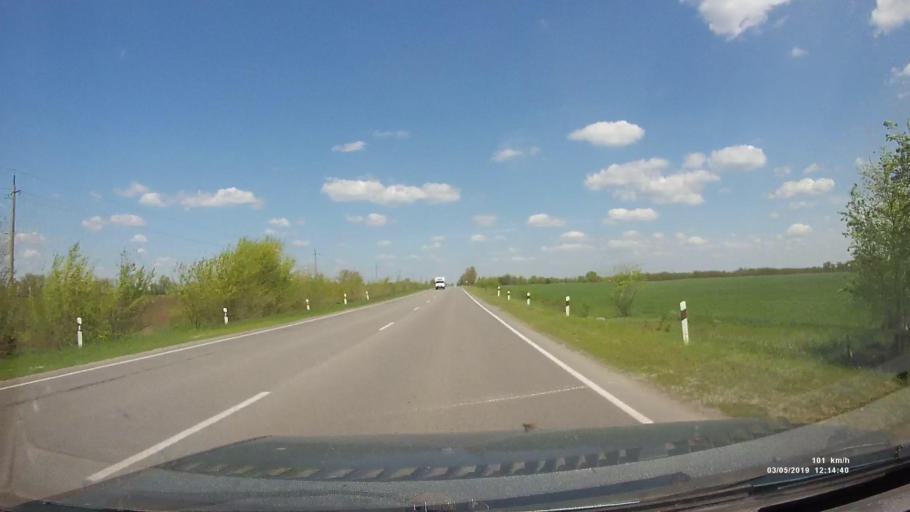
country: RU
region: Rostov
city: Melikhovskaya
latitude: 47.3473
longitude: 40.5658
